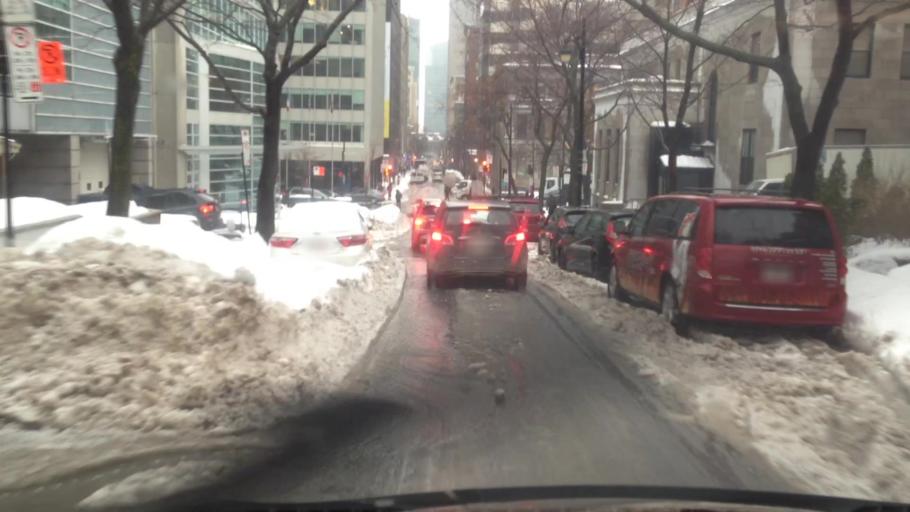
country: CA
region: Quebec
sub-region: Montreal
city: Montreal
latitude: 45.5016
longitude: -73.5783
